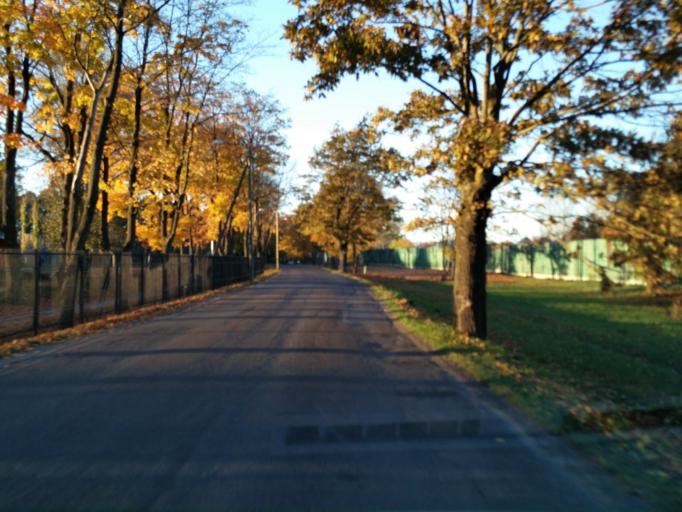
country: EE
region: Tartu
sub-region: Tartu linn
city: Tartu
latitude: 58.3663
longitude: 26.7158
